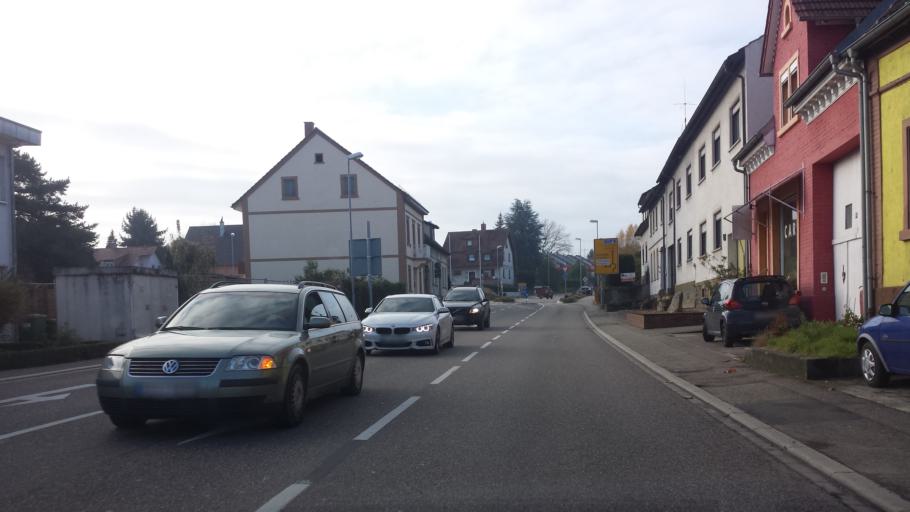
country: DE
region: Baden-Wuerttemberg
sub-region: Karlsruhe Region
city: Ubstadt-Weiher
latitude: 49.1572
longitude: 8.6288
